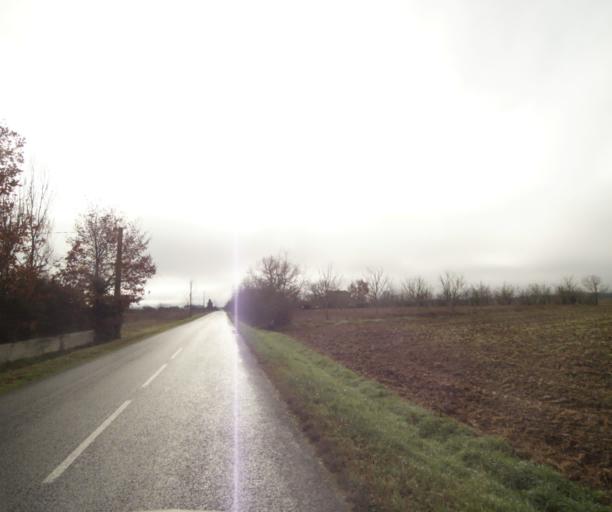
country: FR
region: Midi-Pyrenees
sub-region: Departement du Tarn-et-Garonne
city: Nohic
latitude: 43.8951
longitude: 1.4707
